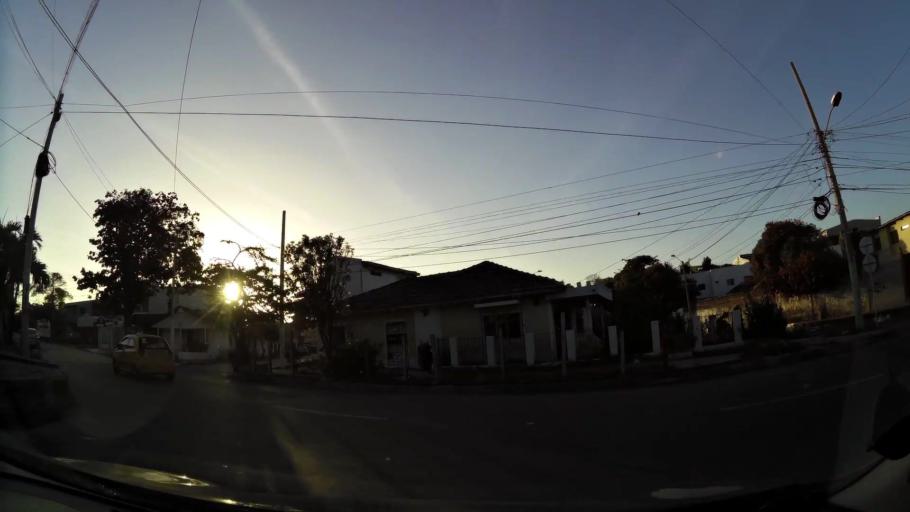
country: CO
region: Atlantico
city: Barranquilla
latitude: 10.9791
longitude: -74.7959
